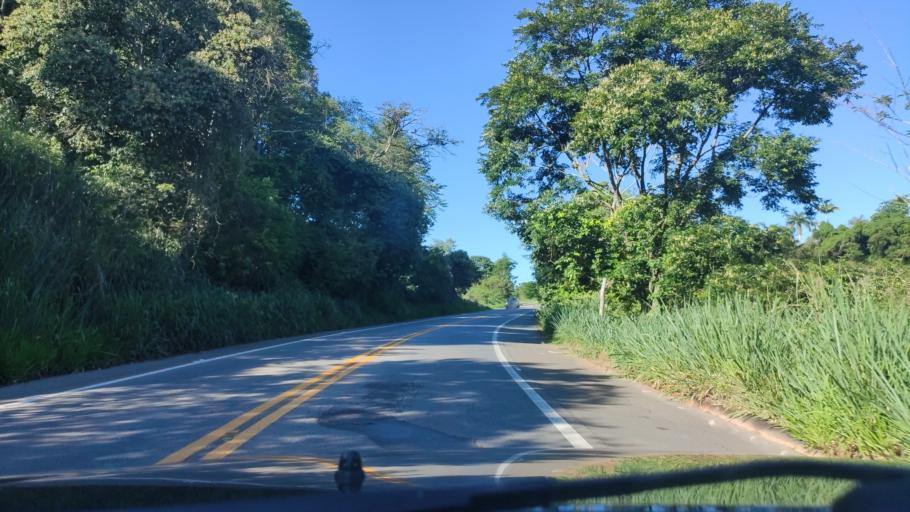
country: BR
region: Sao Paulo
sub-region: Socorro
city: Socorro
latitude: -22.5519
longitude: -46.5810
